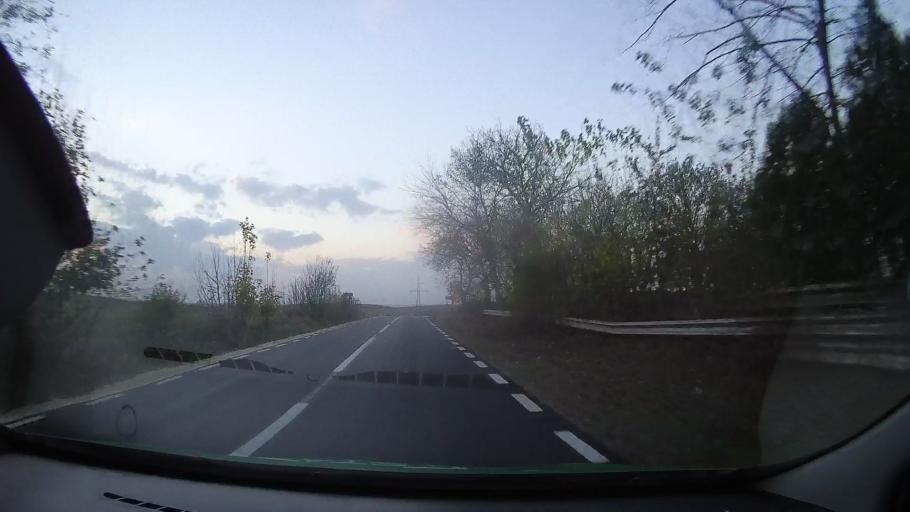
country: RO
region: Constanta
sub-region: Comuna Baneasa
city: Baneasa
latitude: 44.0788
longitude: 27.6942
